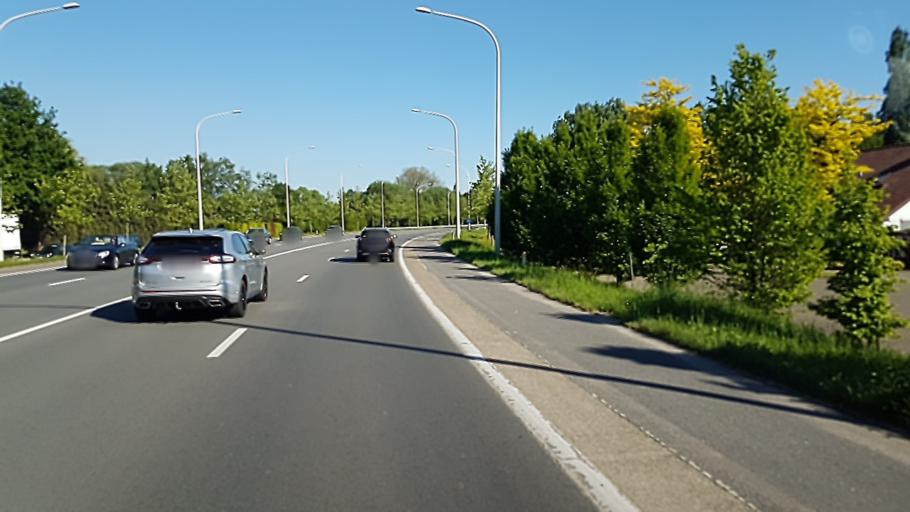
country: BE
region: Flanders
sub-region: Provincie Antwerpen
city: Herentals
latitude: 51.1857
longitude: 4.8451
